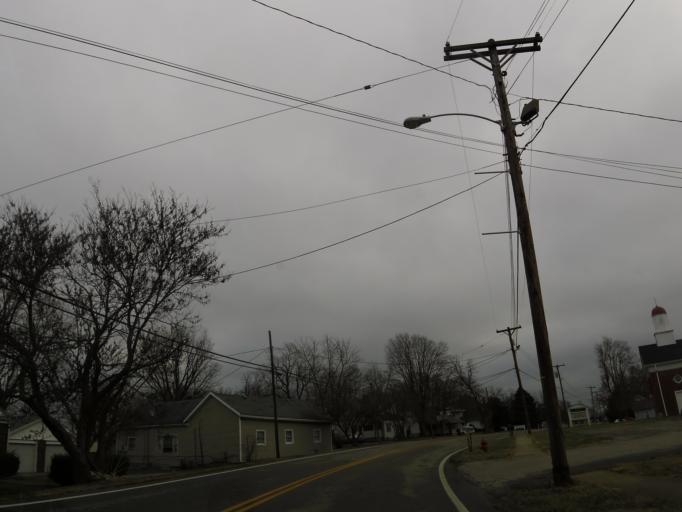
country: US
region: Kentucky
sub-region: Henry County
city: Eminence
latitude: 38.3594
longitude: -85.1058
